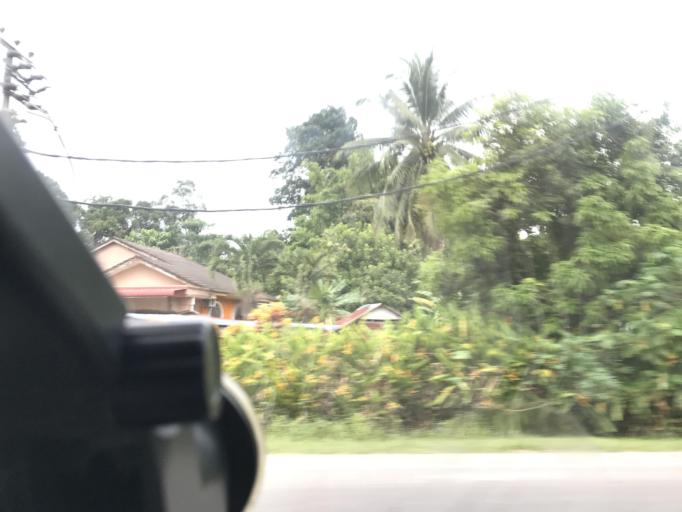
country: MY
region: Kelantan
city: Kota Bharu
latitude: 6.1245
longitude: 102.1746
